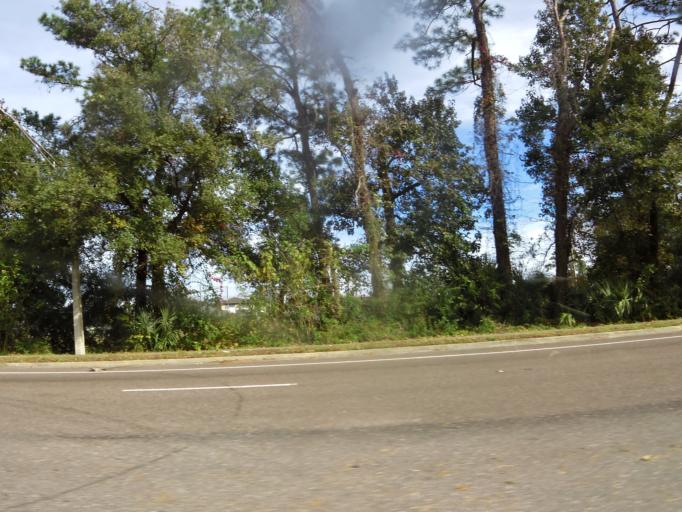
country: US
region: Florida
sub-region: Duval County
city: Jacksonville
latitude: 30.2434
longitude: -81.6090
